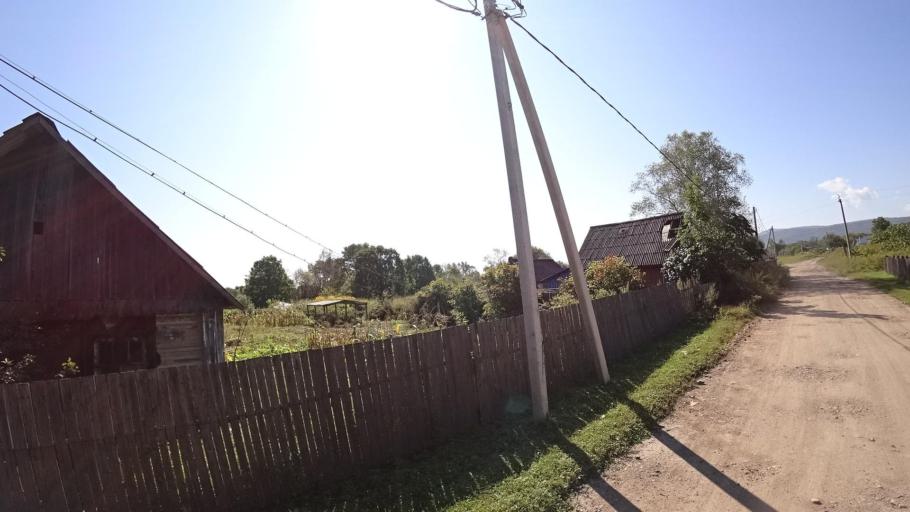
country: RU
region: Jewish Autonomous Oblast
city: Bira
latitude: 48.9947
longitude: 132.4600
